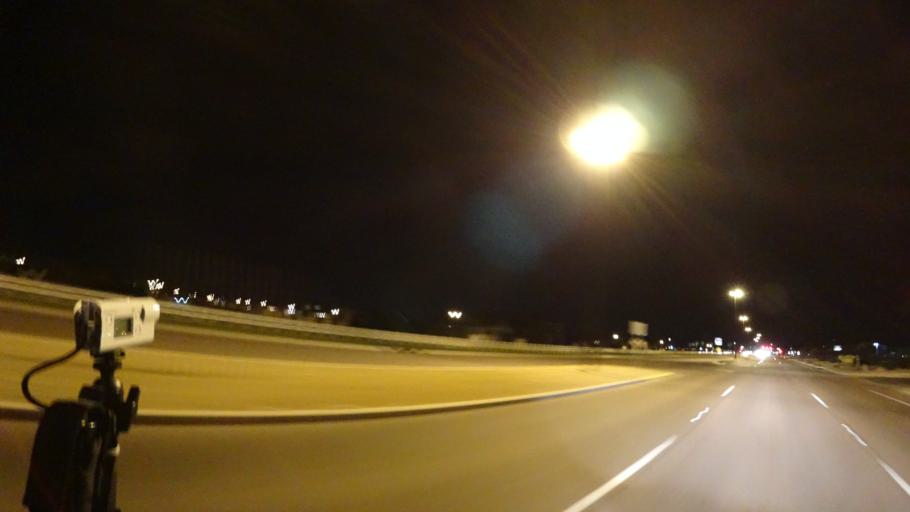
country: US
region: Arizona
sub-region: Maricopa County
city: Gilbert
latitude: 33.3358
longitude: -111.7263
